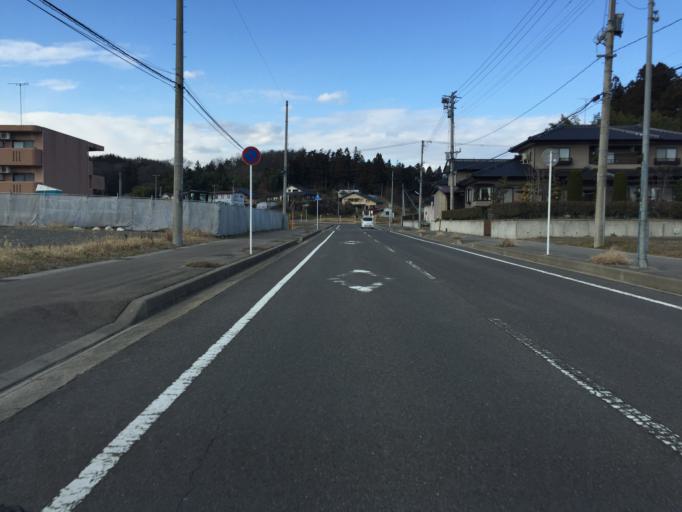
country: JP
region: Fukushima
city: Fukushima-shi
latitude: 37.6819
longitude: 140.4519
